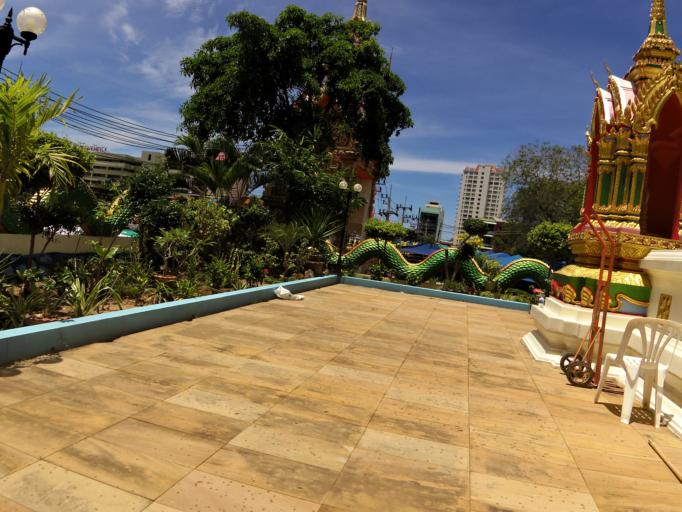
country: TH
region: Phuket
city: Ban Karon
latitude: 7.8479
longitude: 98.2985
